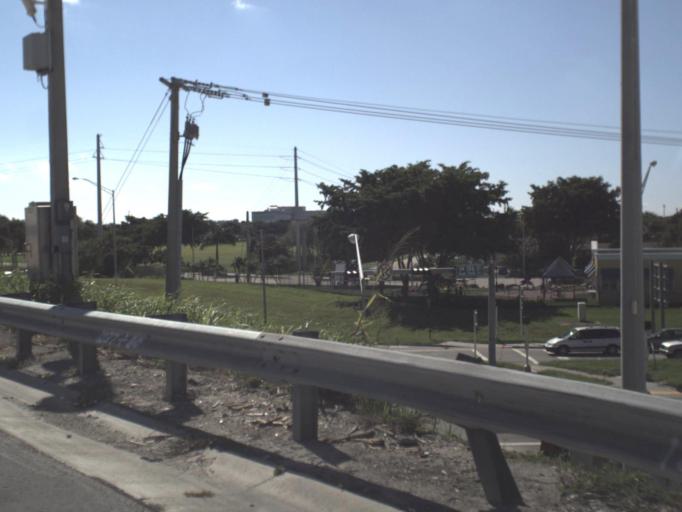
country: US
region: Florida
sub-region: Miami-Dade County
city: South Miami Heights
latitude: 25.5957
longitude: -80.3729
